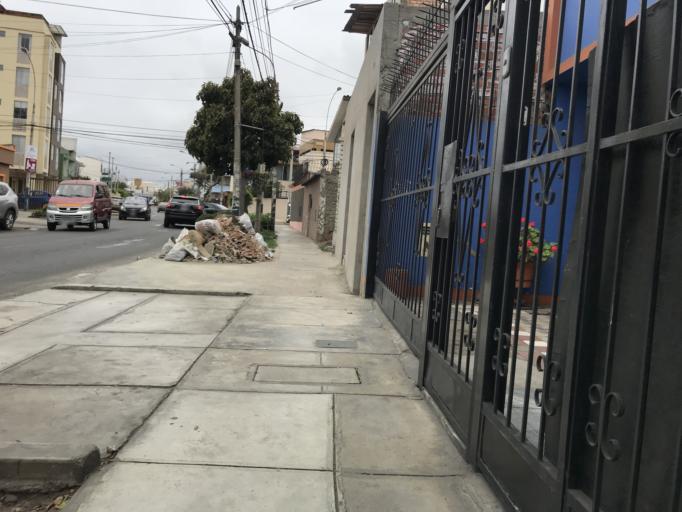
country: PE
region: Lima
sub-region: Lima
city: San Isidro
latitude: -12.0748
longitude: -77.0729
